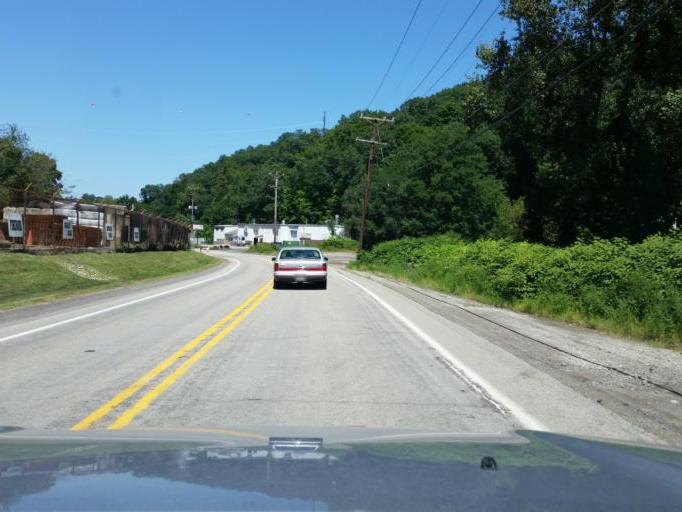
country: US
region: Pennsylvania
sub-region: Allegheny County
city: Blawnox
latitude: 40.4822
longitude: -79.8510
